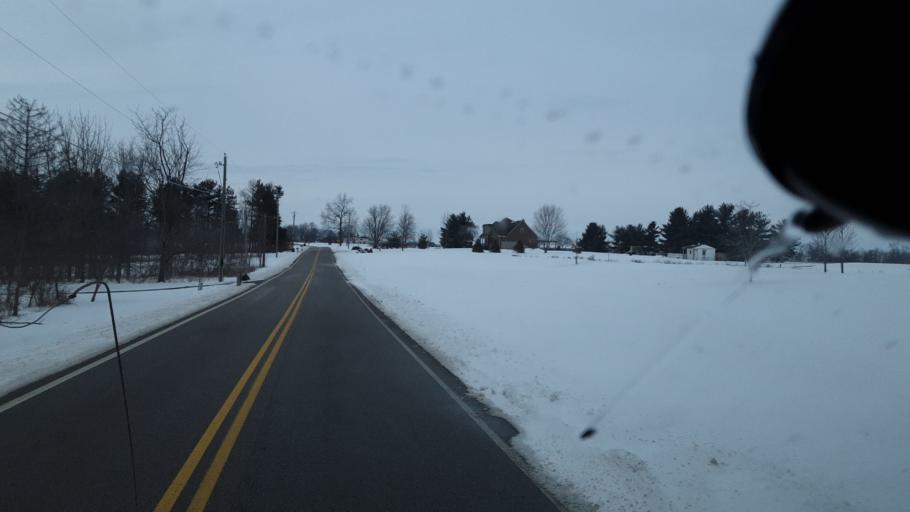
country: US
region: Ohio
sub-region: Madison County
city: Plain City
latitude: 40.1396
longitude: -83.3247
